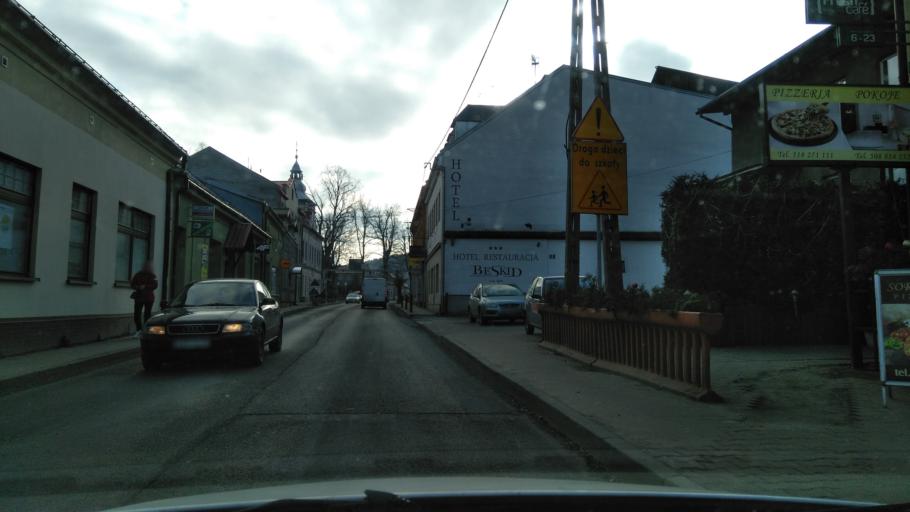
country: PL
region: Silesian Voivodeship
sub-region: Powiat zywiecki
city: Milowka
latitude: 49.5589
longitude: 19.0870
